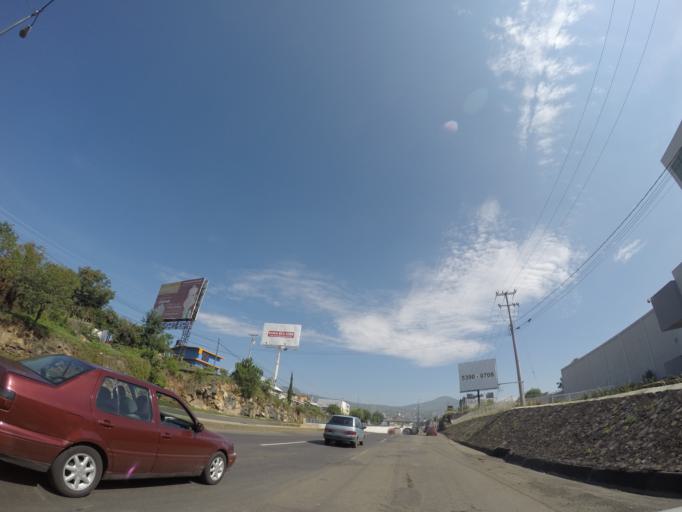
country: MX
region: Michoacan
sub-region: Morelia
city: San Antonio
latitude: 19.6965
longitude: -101.2418
